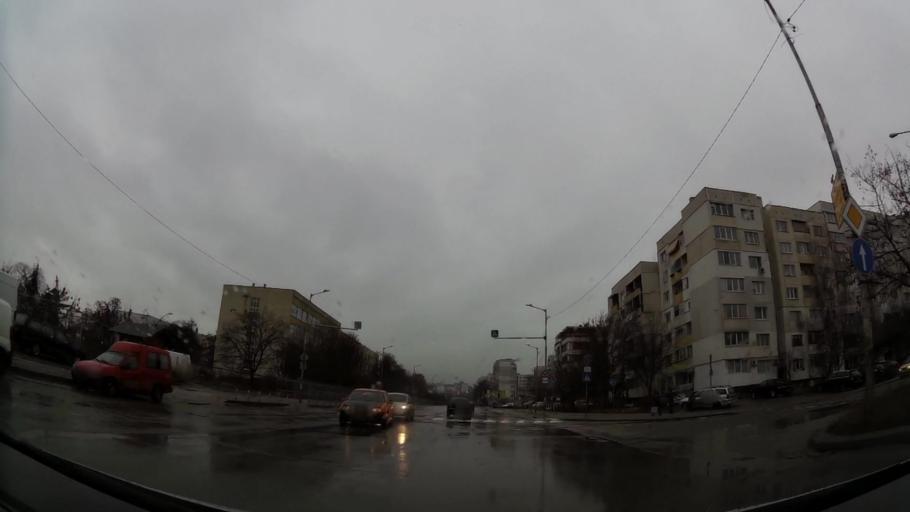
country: BG
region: Sofia-Capital
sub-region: Stolichna Obshtina
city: Sofia
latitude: 42.6353
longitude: 23.3803
